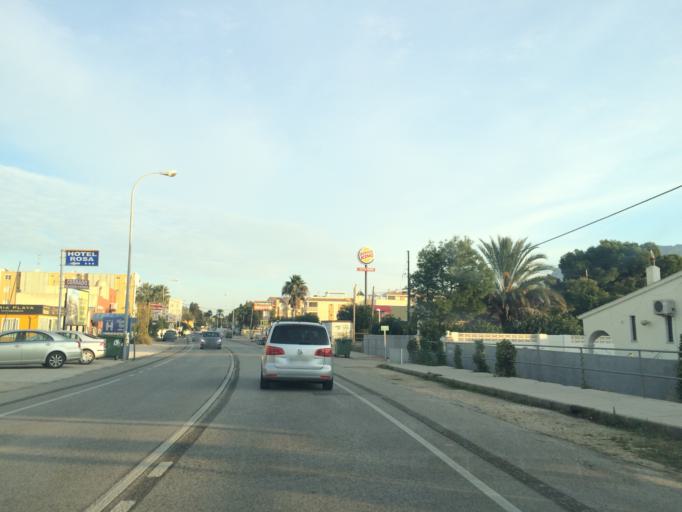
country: ES
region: Valencia
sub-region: Provincia de Alicante
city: Denia
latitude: 38.8500
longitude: 0.0953
